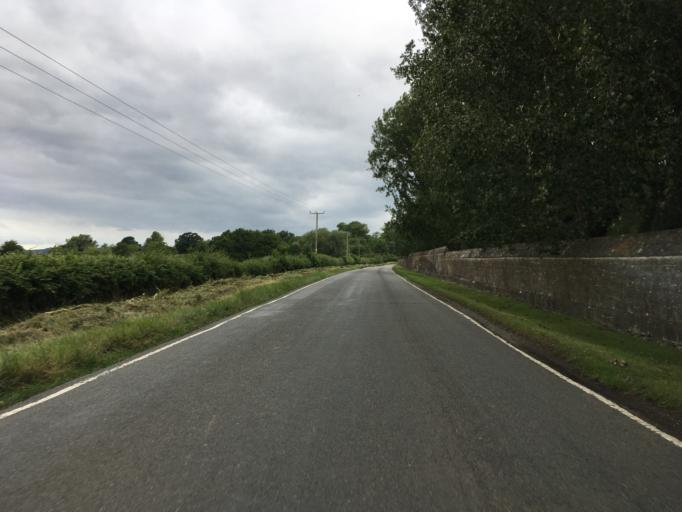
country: GB
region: England
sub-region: Gloucestershire
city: Dursley
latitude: 51.7793
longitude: -2.3834
